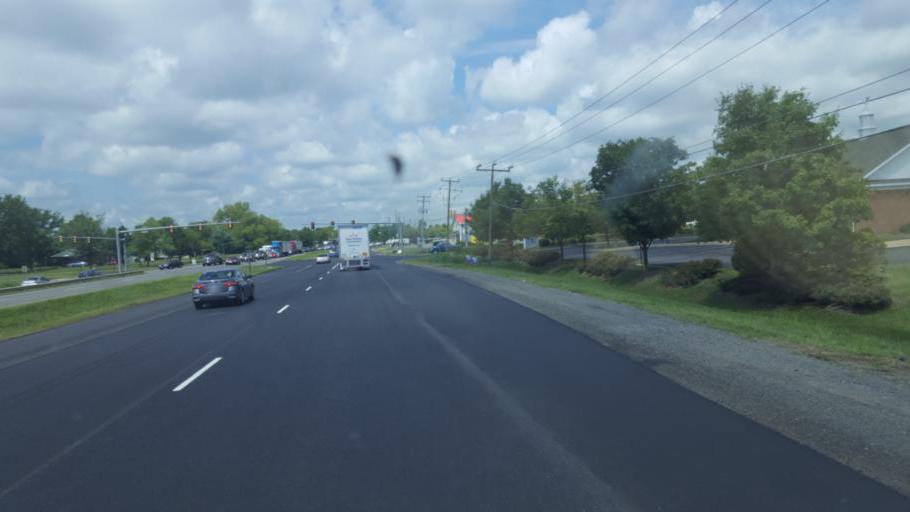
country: US
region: Virginia
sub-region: Fauquier County
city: Bealeton
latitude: 38.5752
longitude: -77.7643
